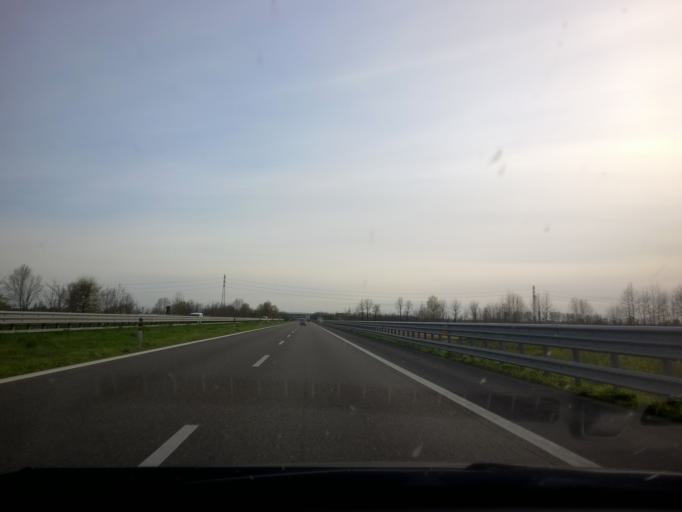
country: IT
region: Lombardy
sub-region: Provincia di Brescia
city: San Gervasio Bresciano
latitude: 45.3197
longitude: 10.1468
